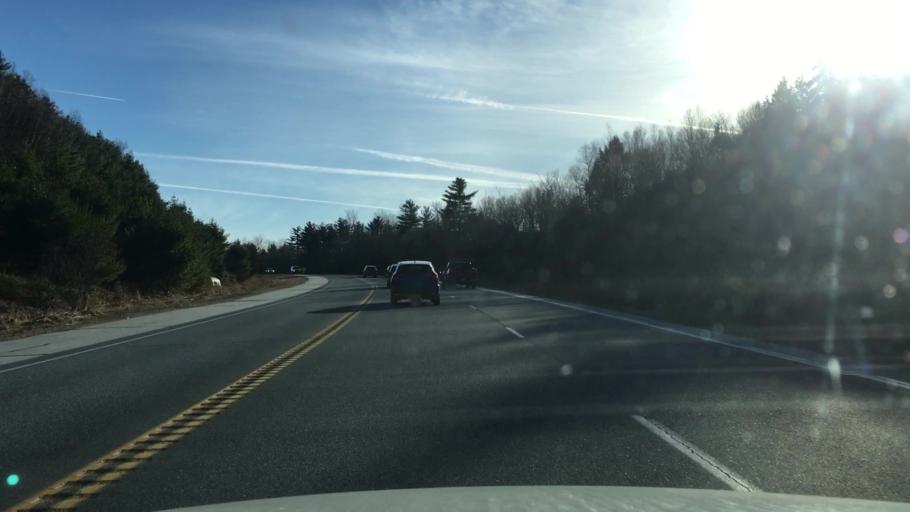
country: US
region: Maine
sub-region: Hancock County
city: Dedham
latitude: 44.6750
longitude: -68.5787
